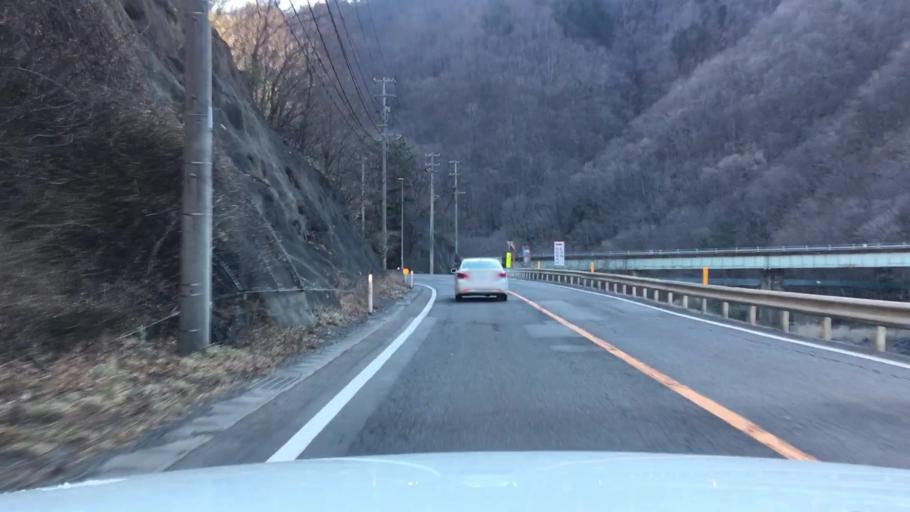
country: JP
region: Iwate
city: Miyako
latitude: 39.5978
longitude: 141.7589
